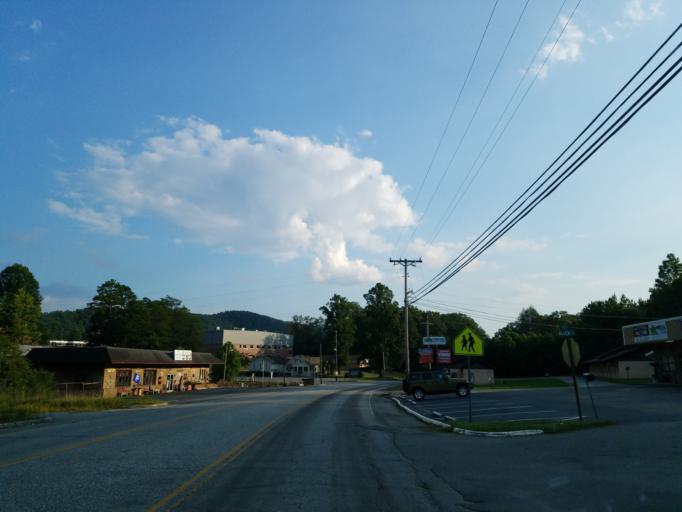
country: US
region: Georgia
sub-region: Fannin County
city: Blue Ridge
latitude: 34.8549
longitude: -84.3302
